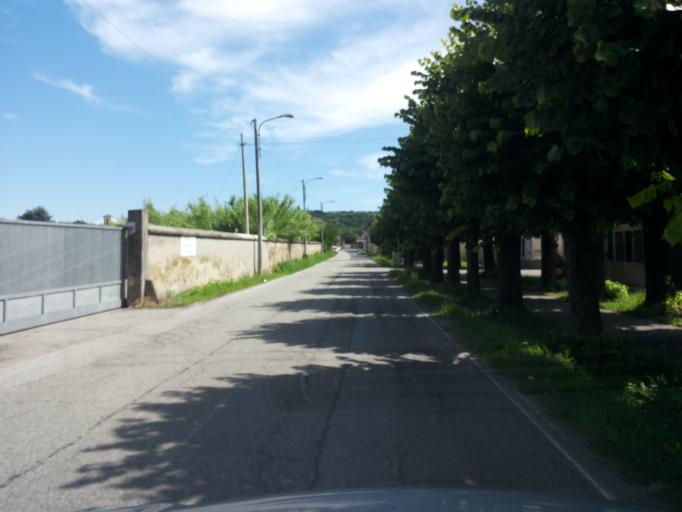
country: IT
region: Piedmont
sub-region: Provincia di Alessandria
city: Morano sul Po
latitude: 45.1670
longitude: 8.3663
